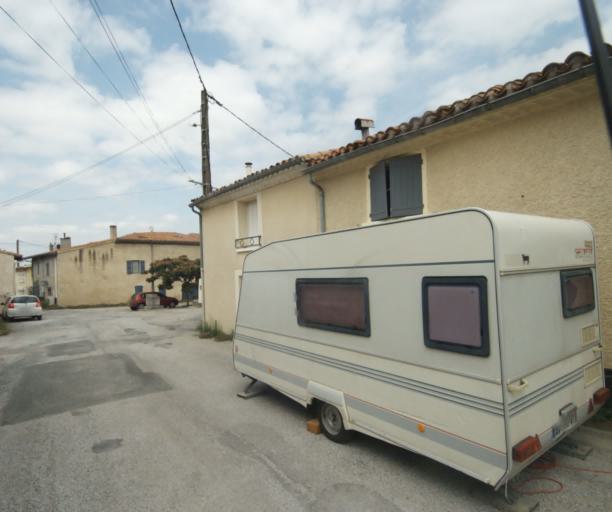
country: FR
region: Midi-Pyrenees
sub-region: Departement de la Haute-Garonne
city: Revel
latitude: 43.4491
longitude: 2.0351
